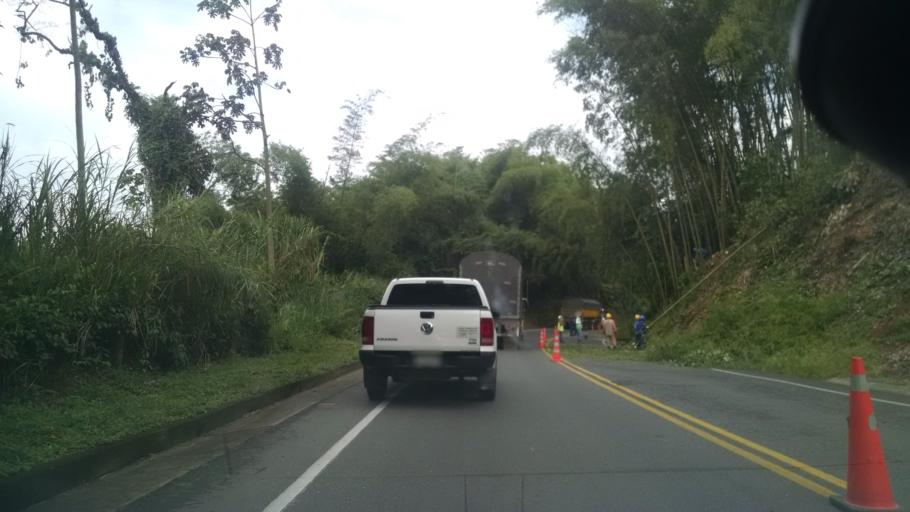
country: CO
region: Caldas
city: Palestina
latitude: 5.0742
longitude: -75.6450
